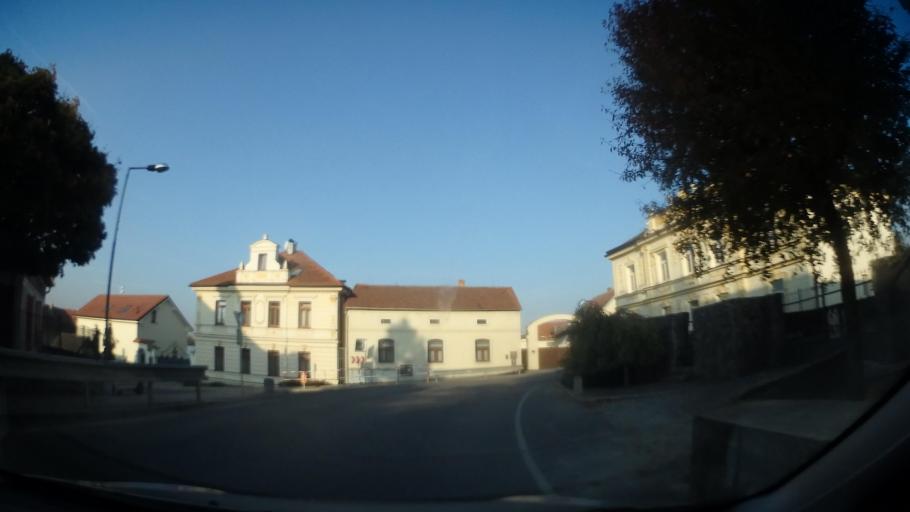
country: CZ
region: Central Bohemia
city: Jirny
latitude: 50.1148
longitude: 14.6991
